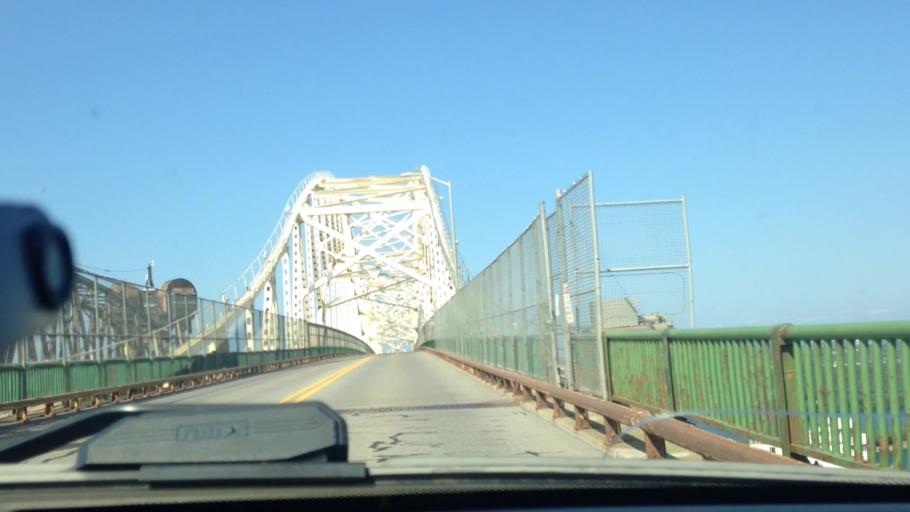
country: US
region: Michigan
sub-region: Chippewa County
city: Sault Ste. Marie
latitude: 46.5012
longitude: -84.3637
